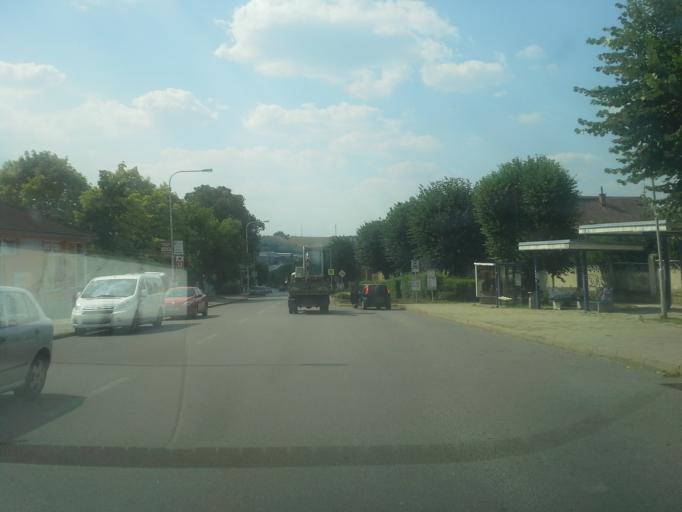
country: CZ
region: South Moravian
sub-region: Okres Blansko
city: Boskovice
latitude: 49.4908
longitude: 16.6613
